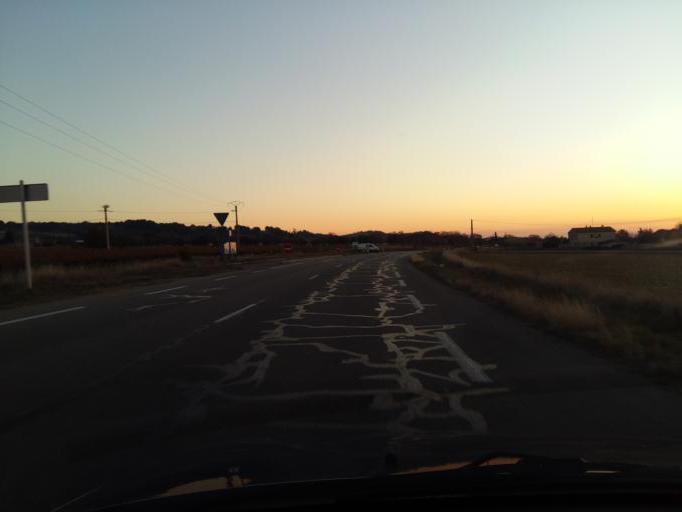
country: FR
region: Provence-Alpes-Cote d'Azur
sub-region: Departement du Vaucluse
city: Valreas
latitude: 44.3671
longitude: 4.9778
